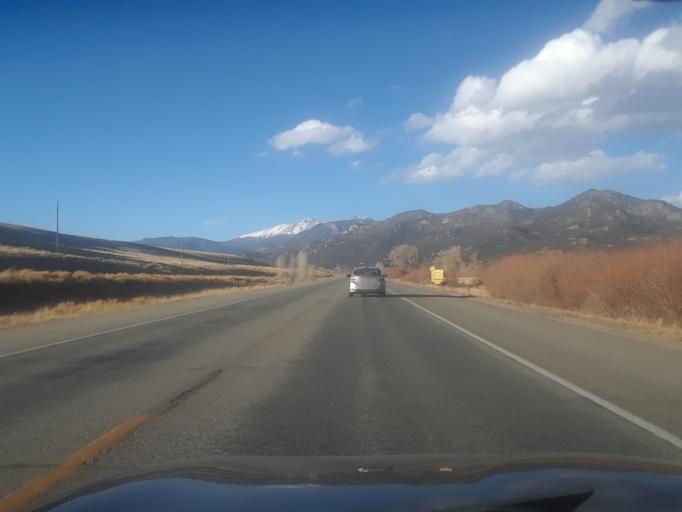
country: US
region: Colorado
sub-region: Chaffee County
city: Buena Vista
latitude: 38.7965
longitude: -106.1141
